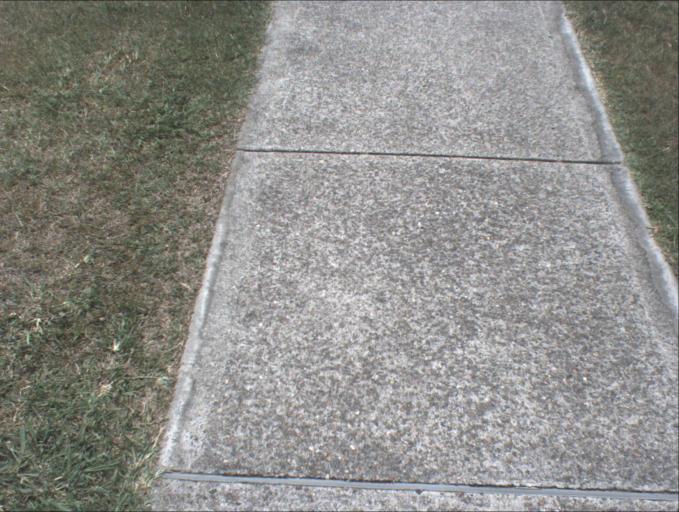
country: AU
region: Queensland
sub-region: Logan
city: Windaroo
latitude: -27.7374
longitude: 153.1895
